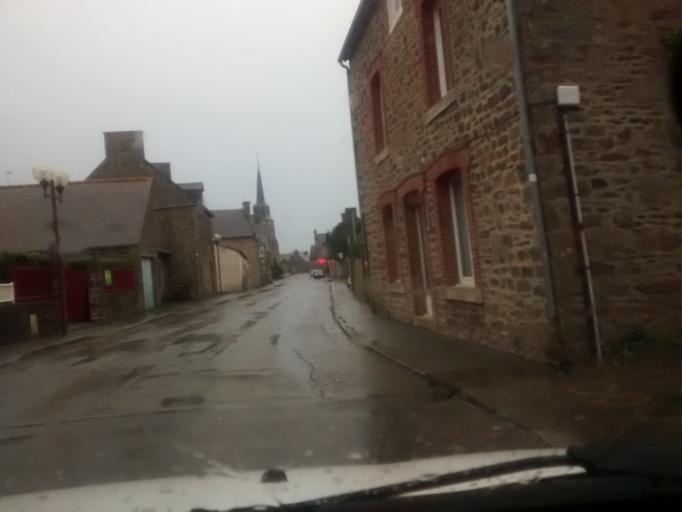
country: FR
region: Brittany
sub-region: Departement d'Ille-et-Vilaine
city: La Gouesniere
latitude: 48.5767
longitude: -1.8836
